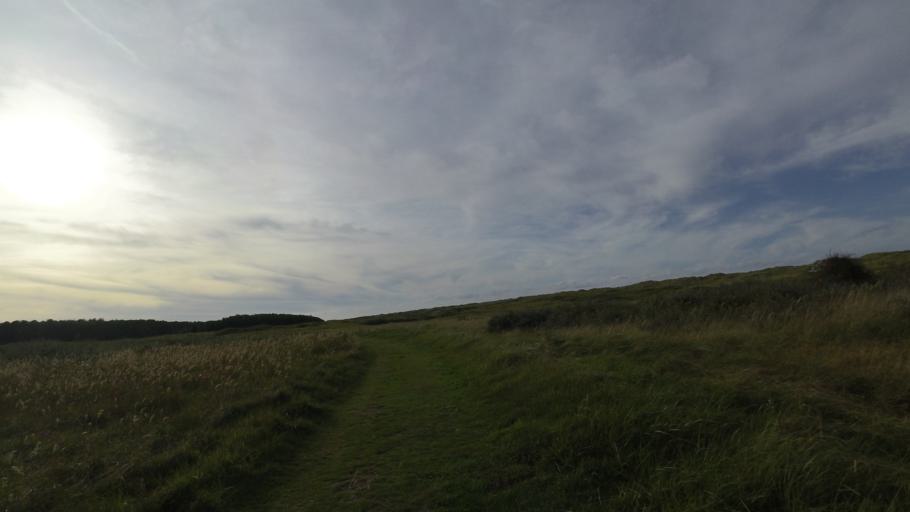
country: NL
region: Friesland
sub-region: Gemeente Ameland
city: Nes
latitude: 53.4596
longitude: 5.8263
